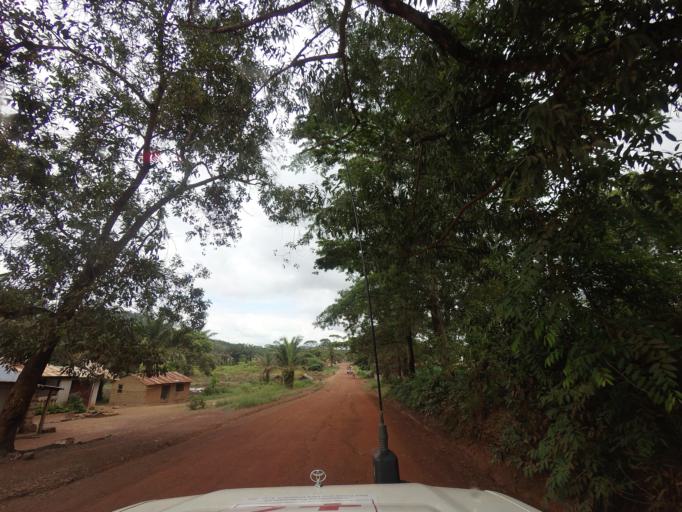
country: LR
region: Nimba
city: Sanniquellie
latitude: 7.3217
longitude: -8.9669
